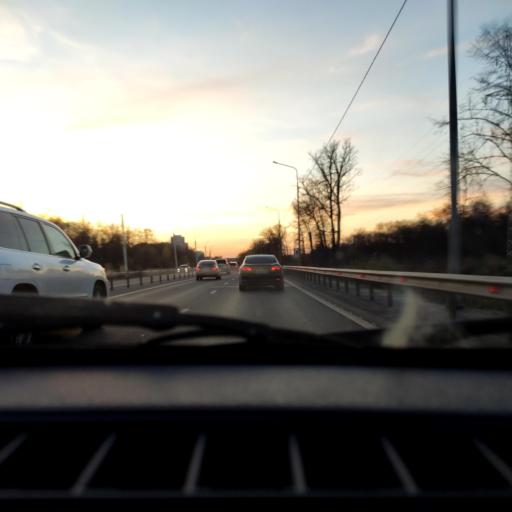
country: RU
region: Bashkortostan
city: Ufa
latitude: 54.6990
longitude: 55.8842
